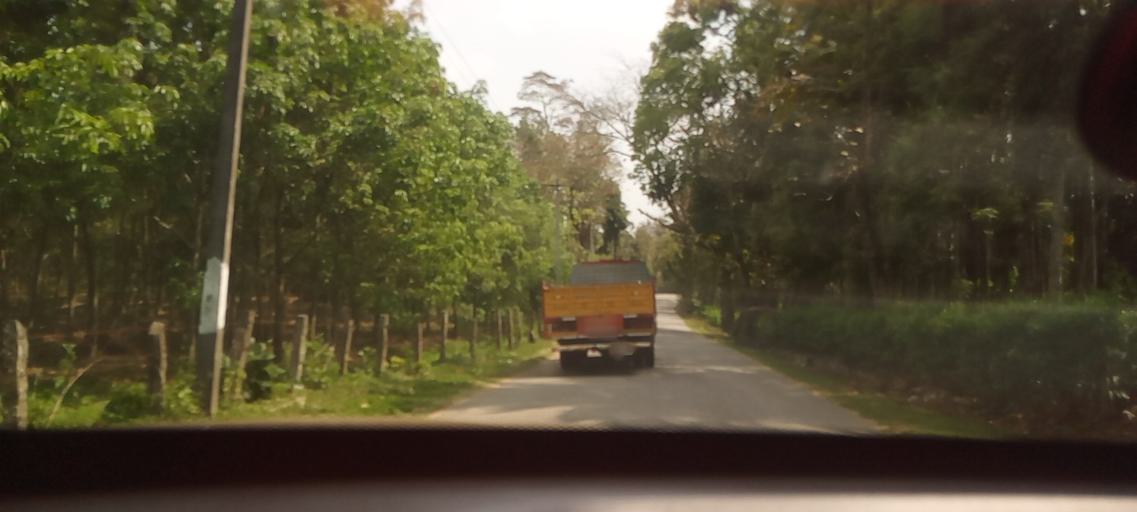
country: IN
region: Karnataka
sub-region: Chikmagalur
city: Mudigere
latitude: 13.3037
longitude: 75.5869
